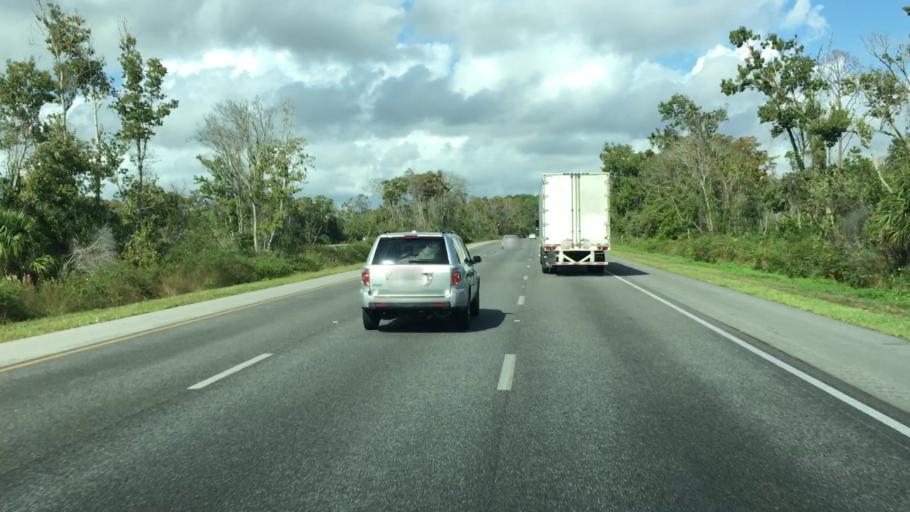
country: US
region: Florida
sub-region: Volusia County
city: Glencoe
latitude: 29.0359
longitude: -81.0027
